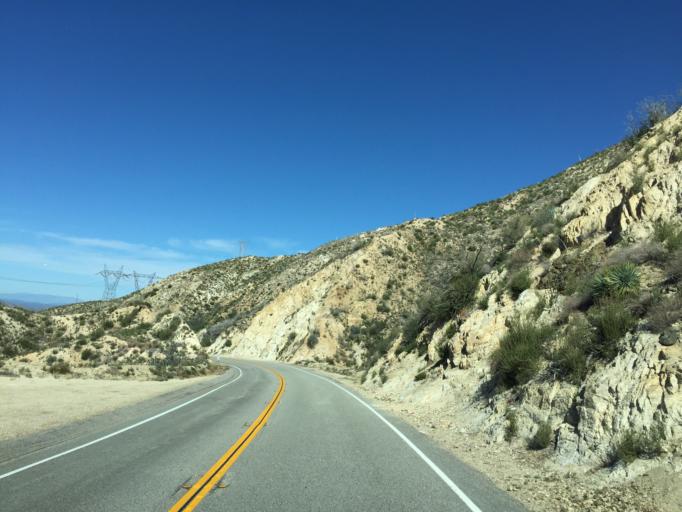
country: US
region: California
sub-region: Los Angeles County
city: Vincent
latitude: 34.4134
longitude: -118.0819
